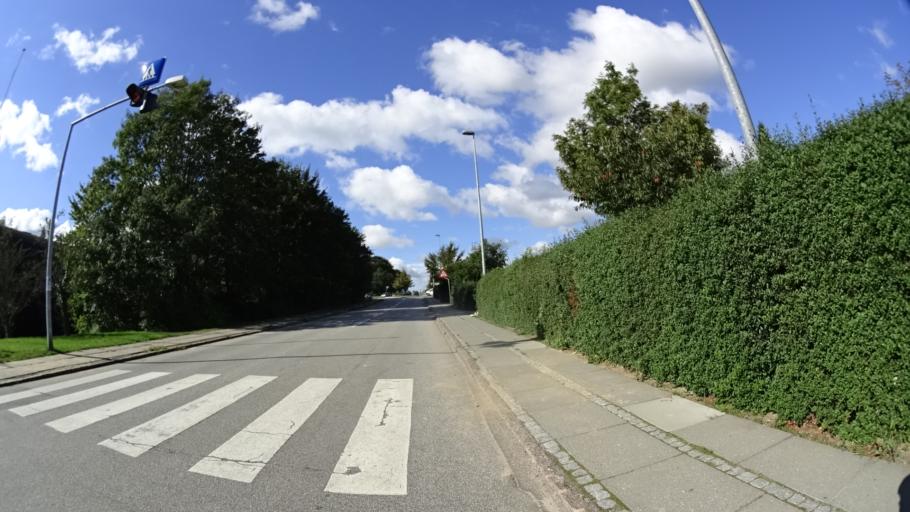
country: DK
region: Central Jutland
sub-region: Arhus Kommune
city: Arhus
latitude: 56.1137
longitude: 10.1920
